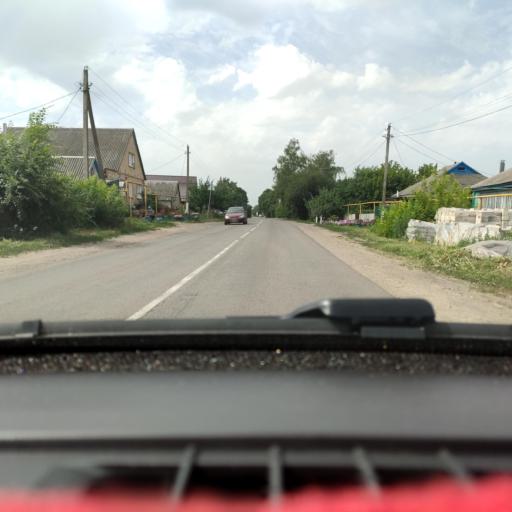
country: RU
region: Voronezj
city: Davydovka
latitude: 51.2066
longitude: 39.5134
